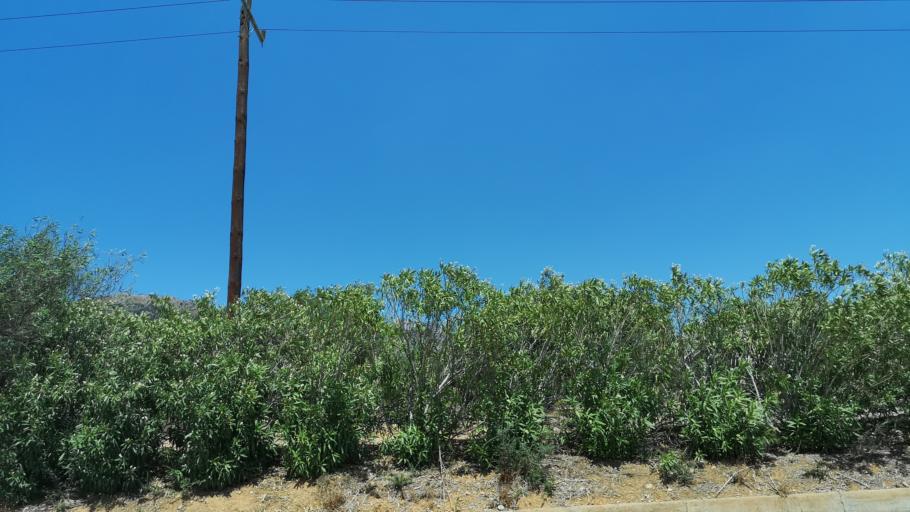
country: GR
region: Crete
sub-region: Nomos Lasithiou
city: Neapoli
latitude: 35.2329
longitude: 25.6514
